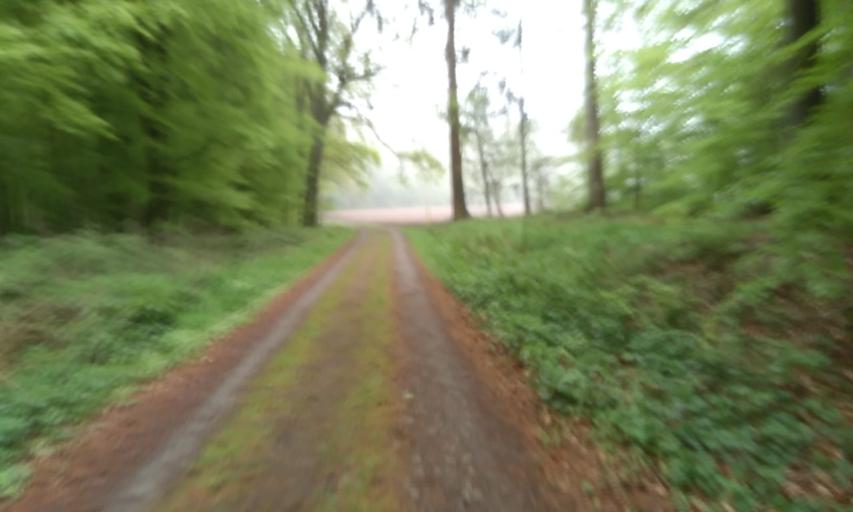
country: DE
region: Lower Saxony
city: Nottensdorf
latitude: 53.4752
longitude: 9.6313
